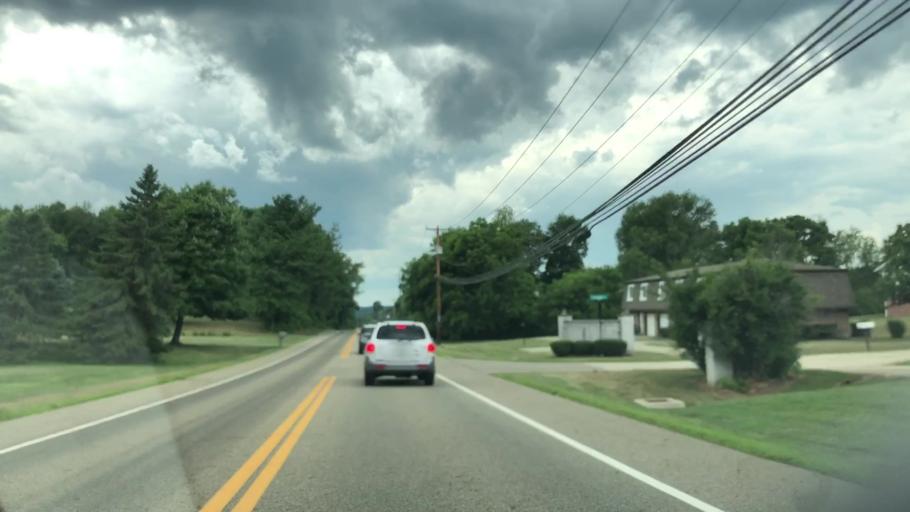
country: US
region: Ohio
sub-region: Summit County
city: Green
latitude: 40.9531
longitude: -81.5024
